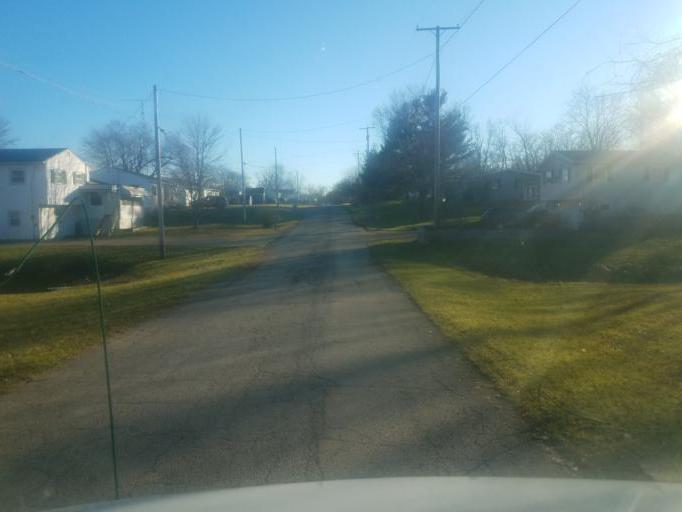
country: US
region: Ohio
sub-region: Richland County
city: Ontario
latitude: 40.7890
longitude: -82.5533
